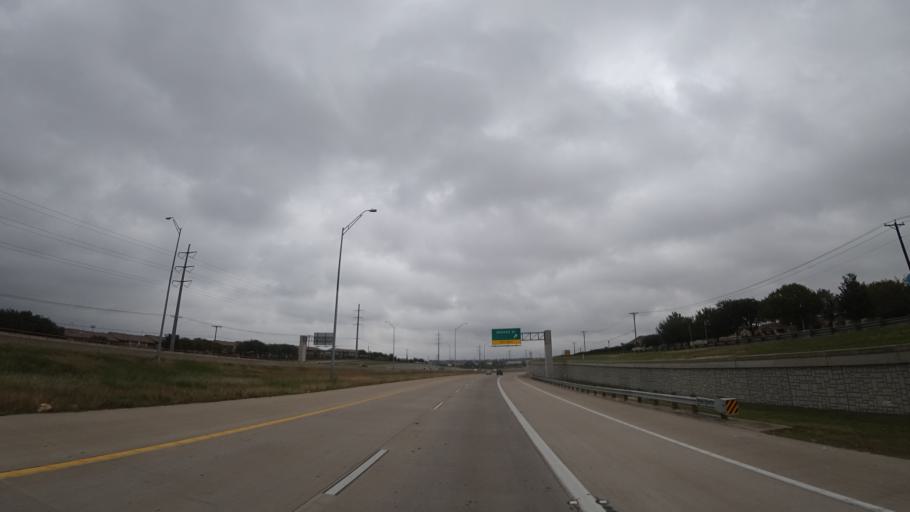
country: US
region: Texas
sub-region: Travis County
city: Windemere
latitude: 30.4883
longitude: -97.6399
